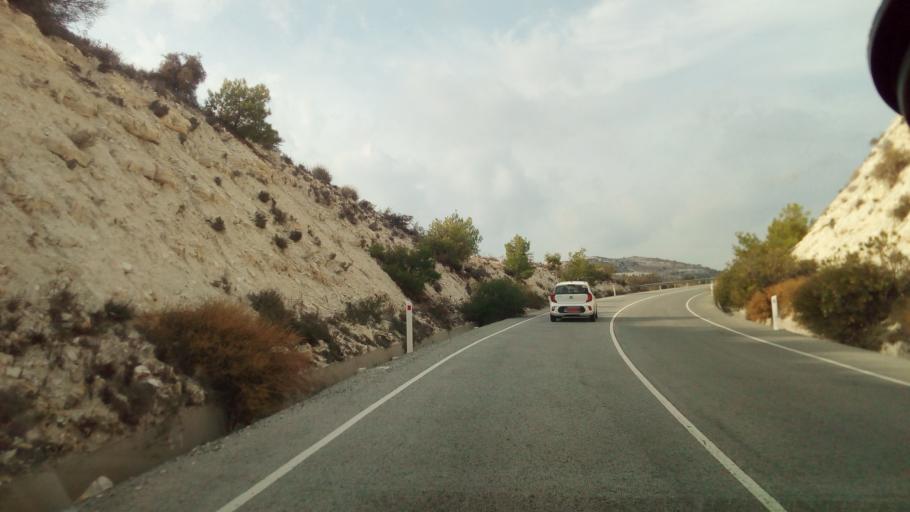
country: CY
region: Larnaka
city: Kofinou
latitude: 34.8450
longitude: 33.3291
